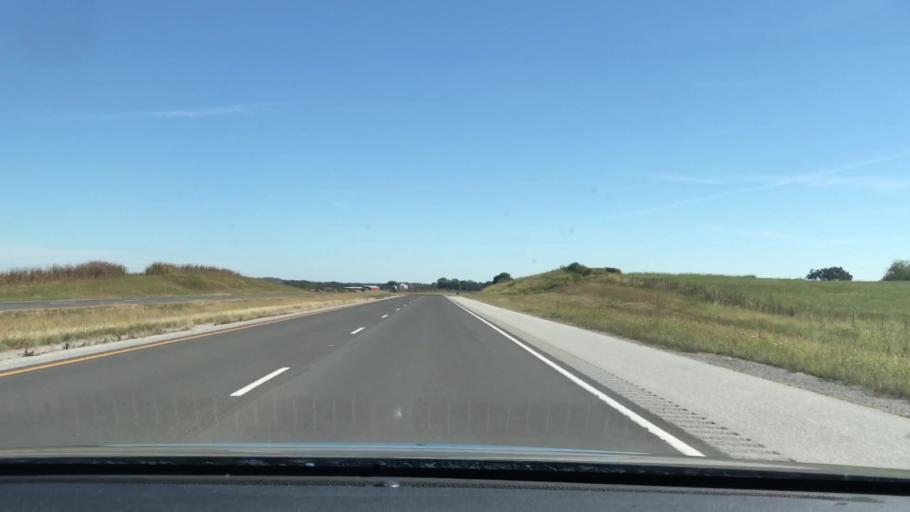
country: US
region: Kentucky
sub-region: Todd County
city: Elkton
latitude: 36.8099
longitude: -87.0408
